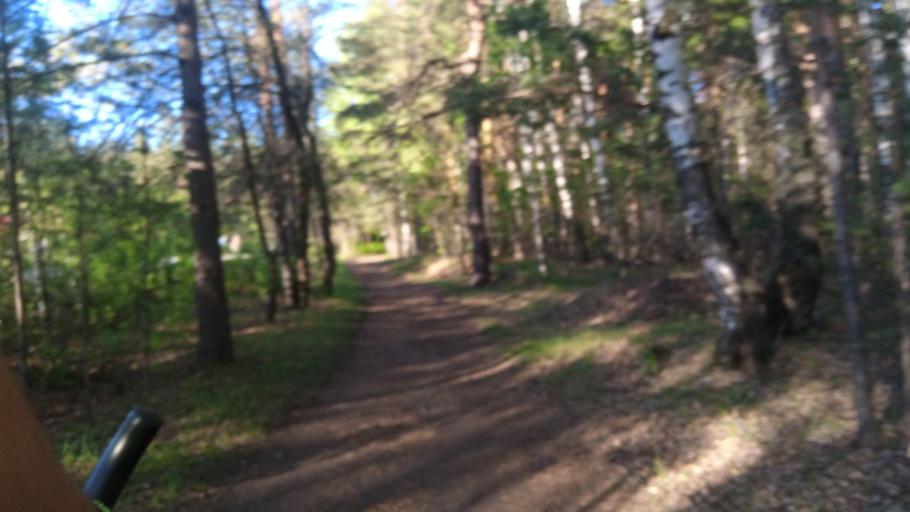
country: RU
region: Chelyabinsk
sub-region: Gorod Chelyabinsk
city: Chelyabinsk
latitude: 55.1519
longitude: 61.3377
